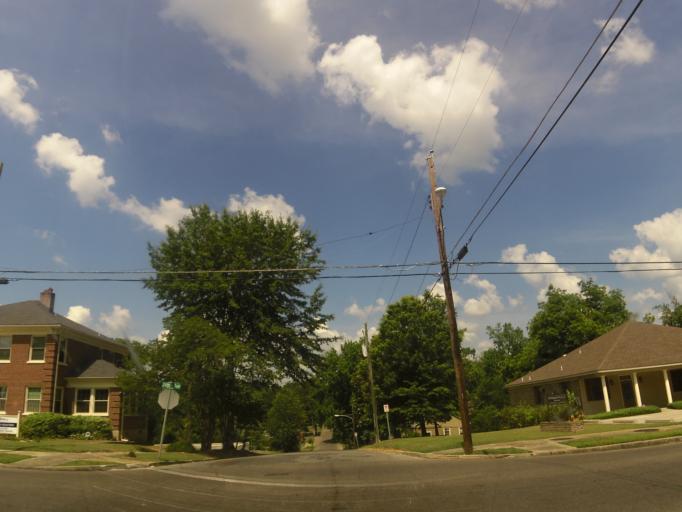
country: US
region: Mississippi
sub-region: Lauderdale County
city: Meridian
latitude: 32.3766
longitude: -88.7025
